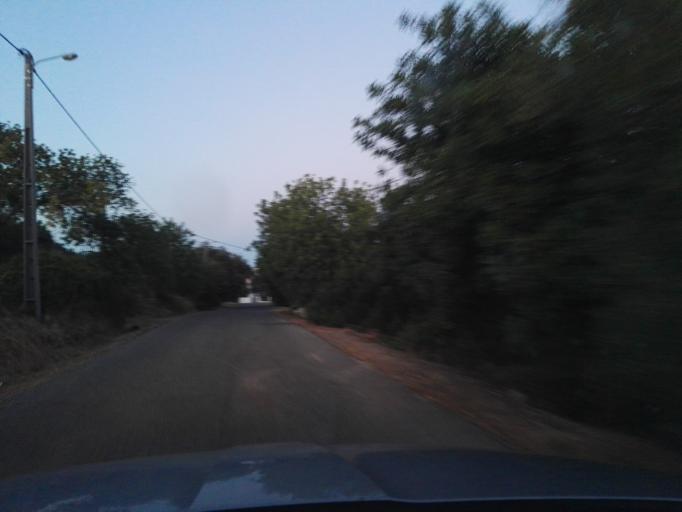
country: PT
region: Faro
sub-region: Sao Bras de Alportel
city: Sao Bras de Alportel
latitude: 37.1571
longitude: -7.9375
